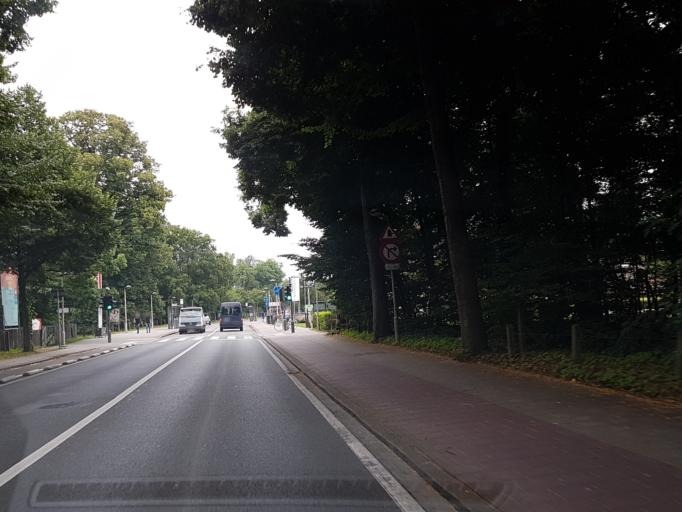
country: BE
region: Flanders
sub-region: Provincie Antwerpen
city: Borsbeek
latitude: 51.2160
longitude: 4.4625
